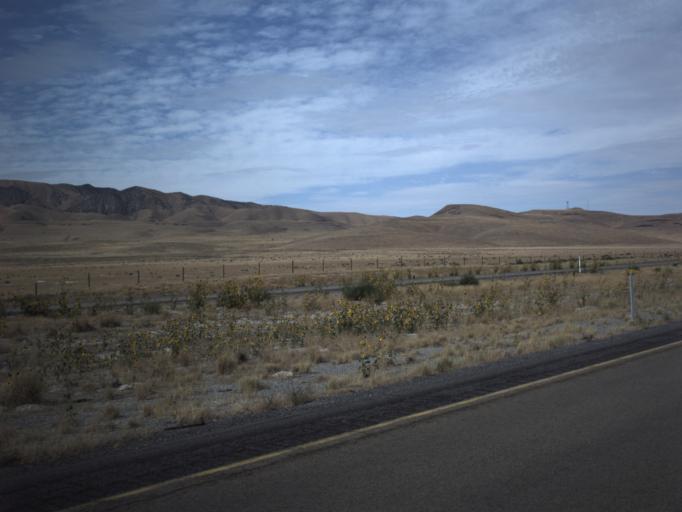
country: US
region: Utah
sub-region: Tooele County
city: Grantsville
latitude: 40.7899
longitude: -112.8306
